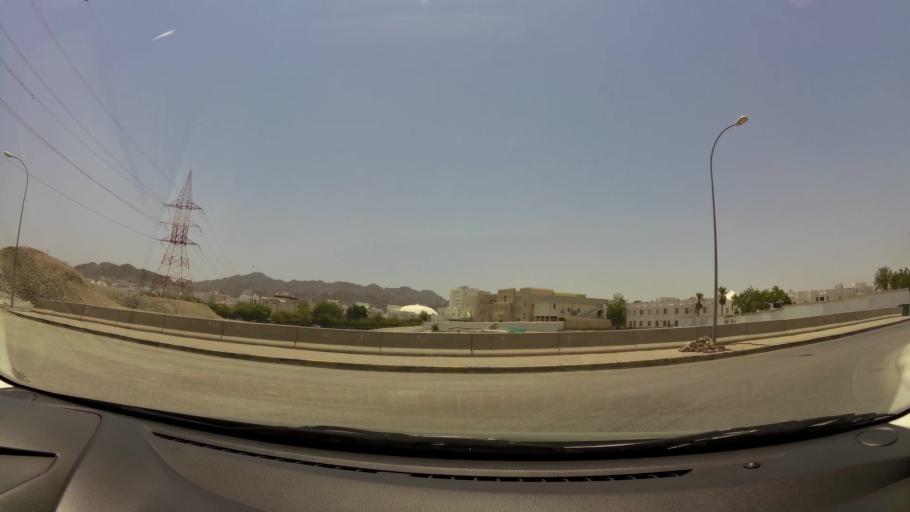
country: OM
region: Muhafazat Masqat
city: Muscat
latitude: 23.6078
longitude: 58.5352
